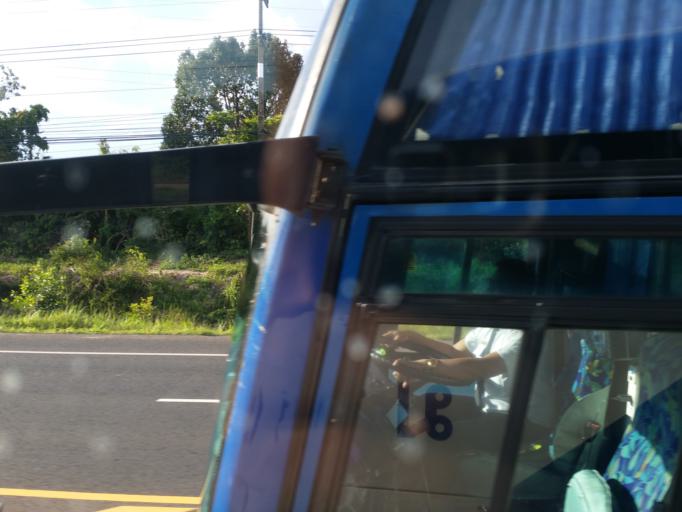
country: TH
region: Changwat Ubon Ratchathani
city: Sirindhorn
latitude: 15.2009
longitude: 105.3842
